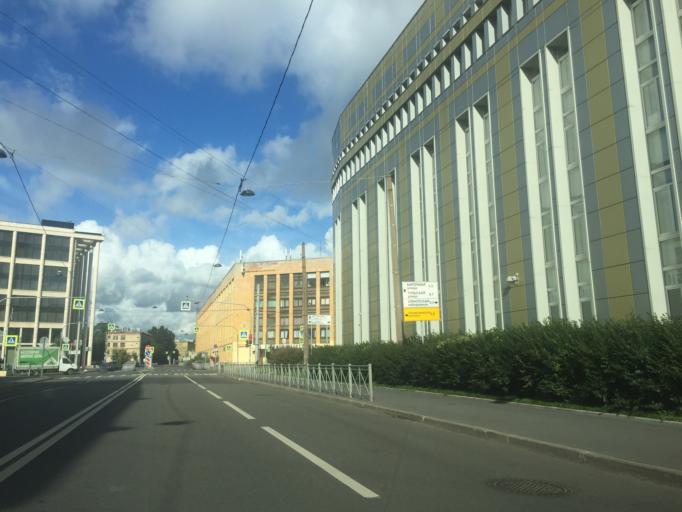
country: RU
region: St.-Petersburg
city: Centralniy
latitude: 59.9369
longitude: 30.3865
